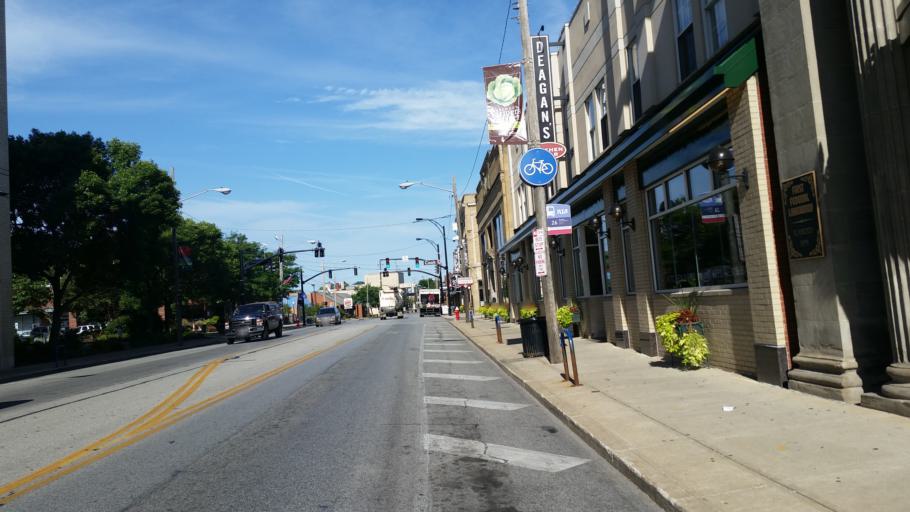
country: US
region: Ohio
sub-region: Cuyahoga County
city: Lakewood
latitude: 41.4852
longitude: -81.7998
